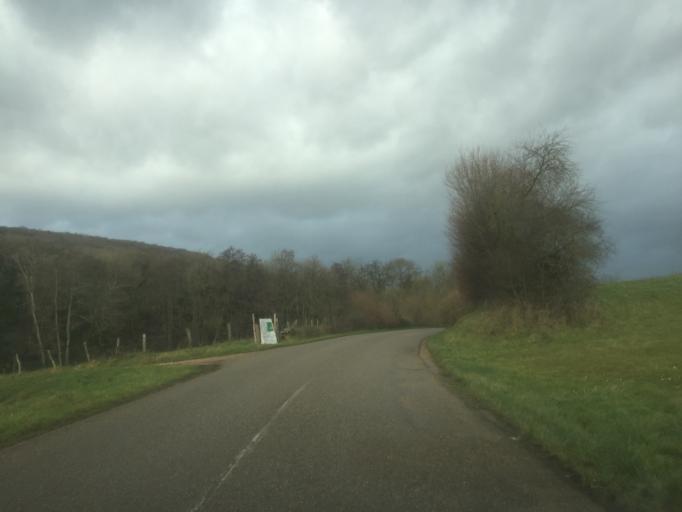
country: FR
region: Franche-Comte
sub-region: Departement du Jura
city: Orchamps
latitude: 47.2200
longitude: 5.6800
